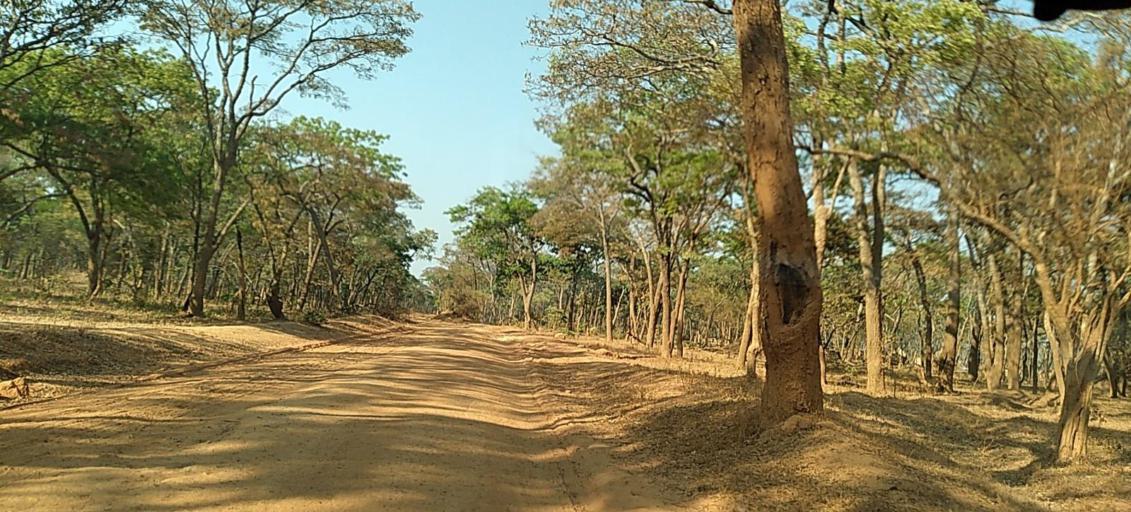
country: ZM
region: North-Western
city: Kasempa
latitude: -13.5977
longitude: 25.9803
